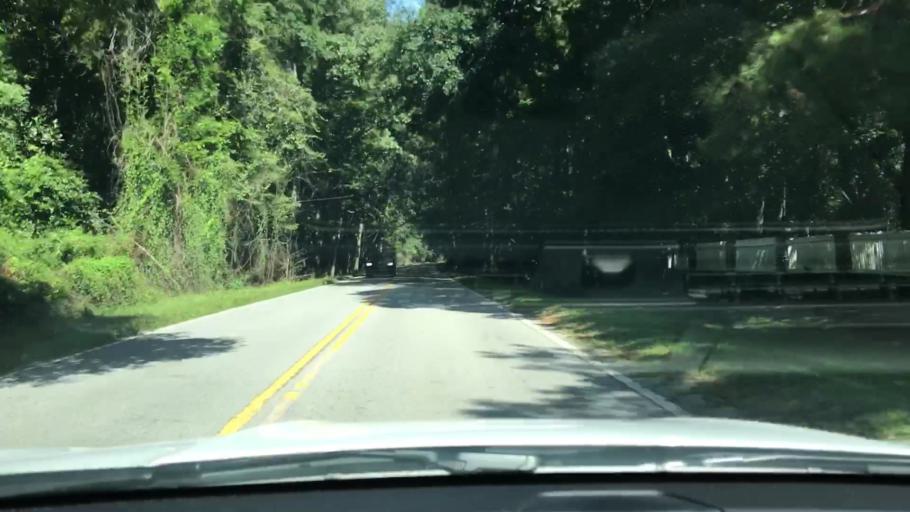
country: US
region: South Carolina
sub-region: Berkeley County
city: Ladson
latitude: 32.8999
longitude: -80.1410
